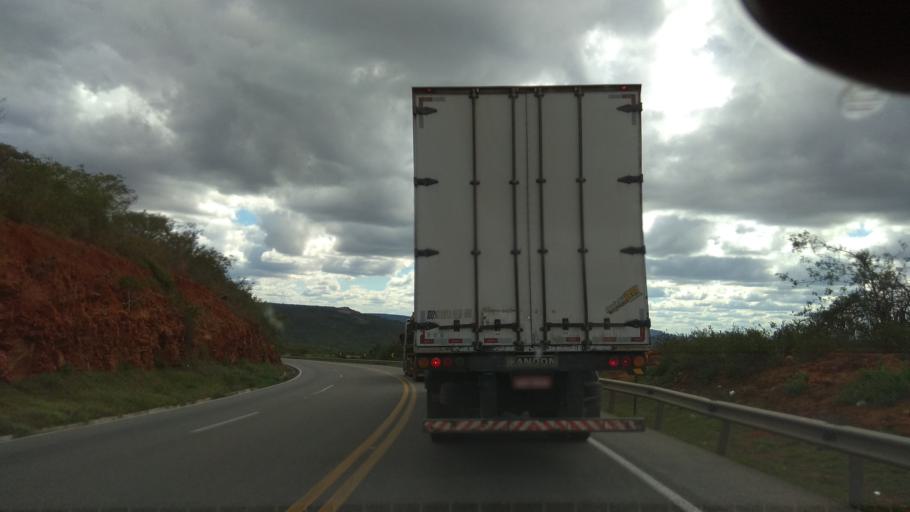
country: BR
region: Bahia
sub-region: Santa Ines
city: Santa Ines
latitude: -13.0447
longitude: -39.9631
